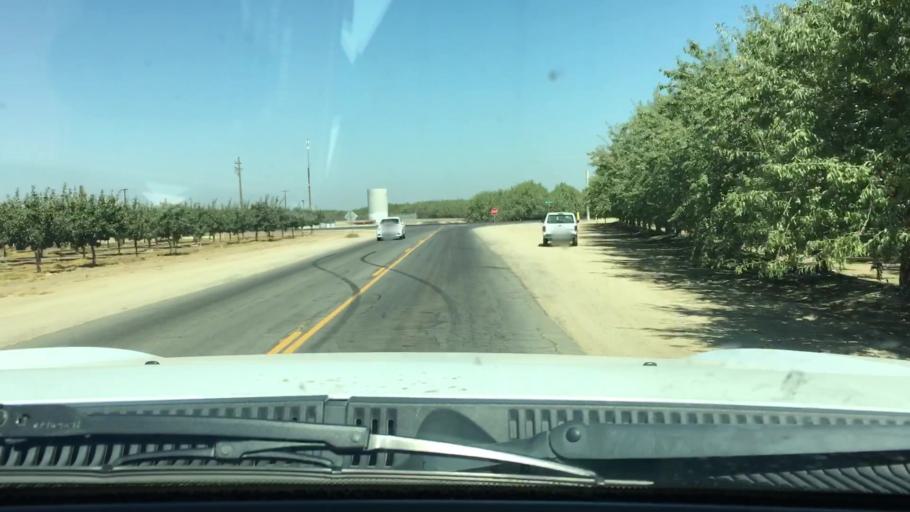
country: US
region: California
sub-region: Kern County
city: Shafter
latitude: 35.5571
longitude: -119.2774
